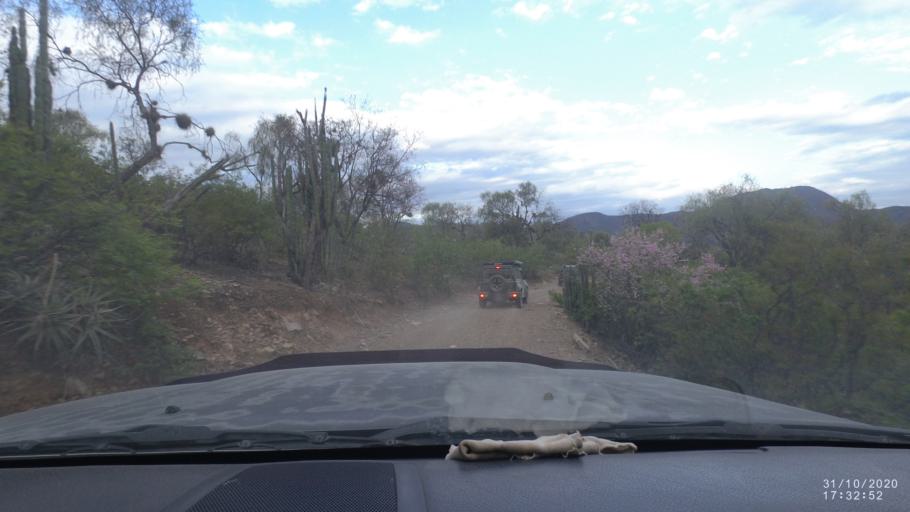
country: BO
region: Chuquisaca
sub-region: Provincia Zudanez
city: Mojocoya
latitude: -18.5987
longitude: -64.5519
